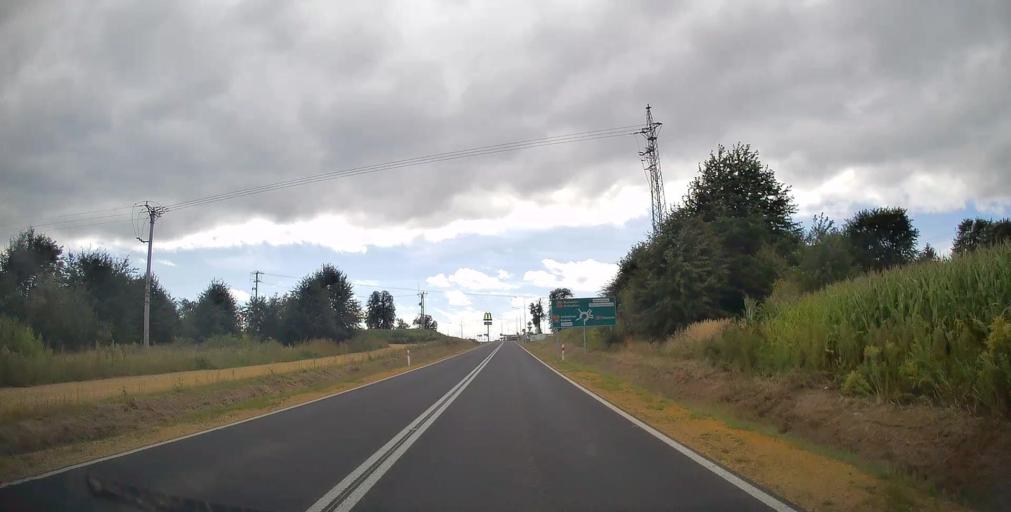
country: PL
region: Lesser Poland Voivodeship
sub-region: Powiat oswiecimski
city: Zator
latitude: 50.0004
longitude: 19.4219
